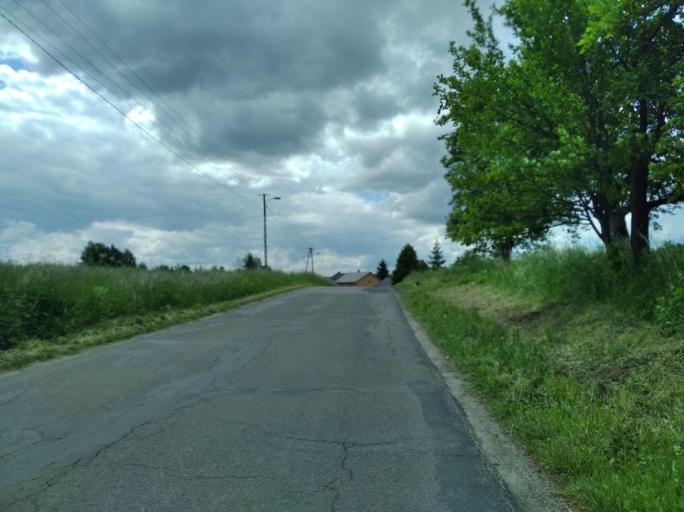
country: PL
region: Subcarpathian Voivodeship
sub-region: Powiat brzozowski
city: Jasionow
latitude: 49.6633
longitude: 21.9746
